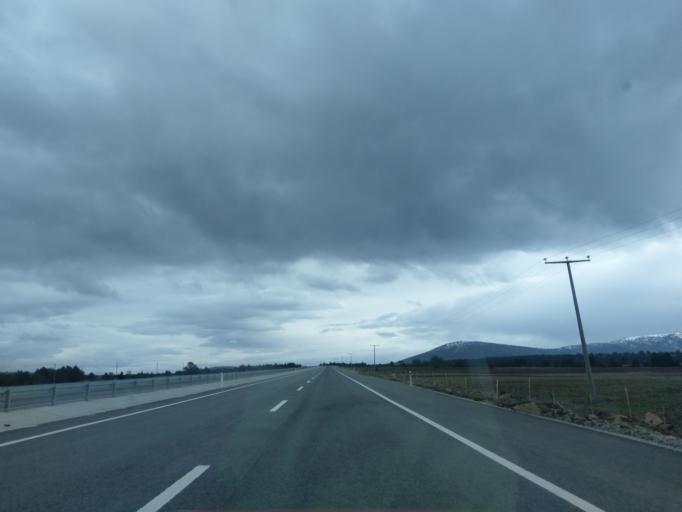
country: TR
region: Kuetahya
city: Cavdarhisar
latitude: 39.2246
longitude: 29.7244
